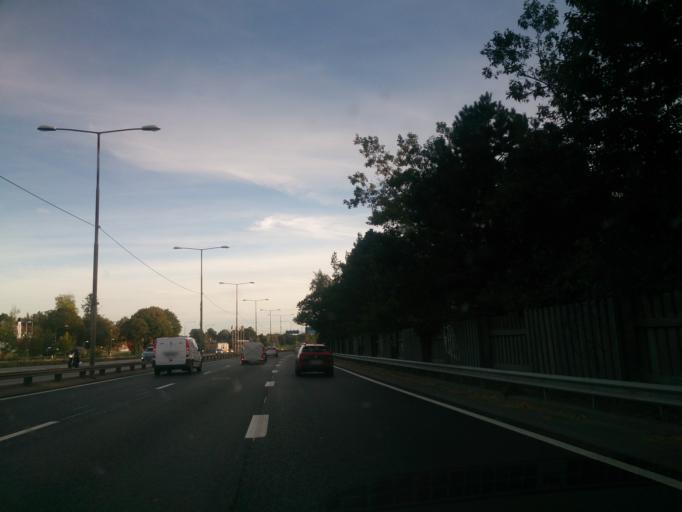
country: SE
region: Stockholm
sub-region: Stockholms Kommun
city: Arsta
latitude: 59.2662
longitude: 18.0972
